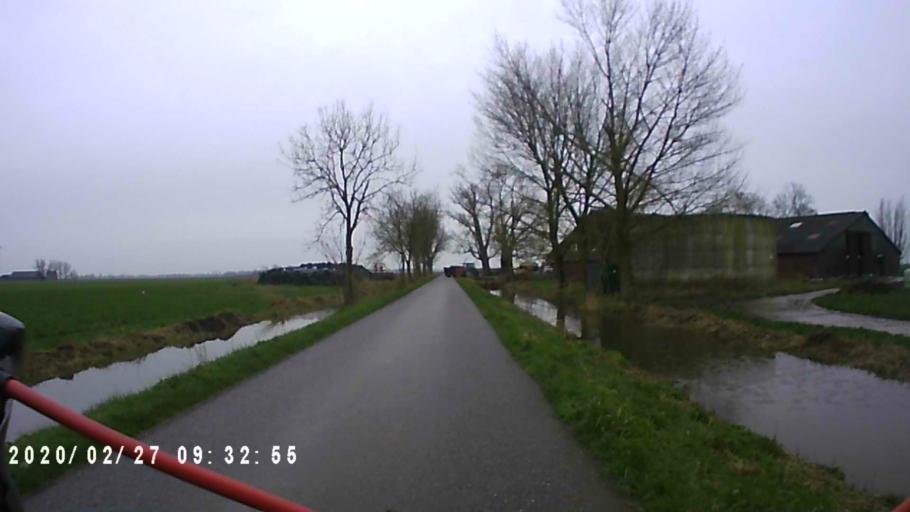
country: NL
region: Groningen
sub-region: Gemeente Zuidhorn
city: Aduard
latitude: 53.2894
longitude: 6.4487
